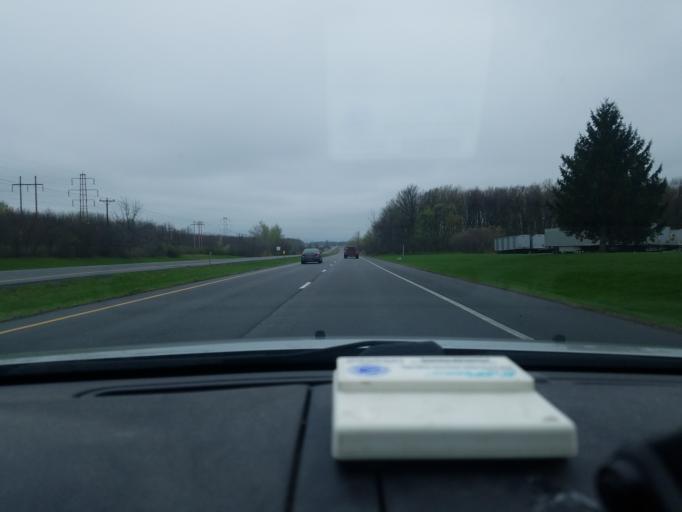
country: US
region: New York
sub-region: Onondaga County
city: East Syracuse
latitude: 43.1078
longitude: -76.0774
